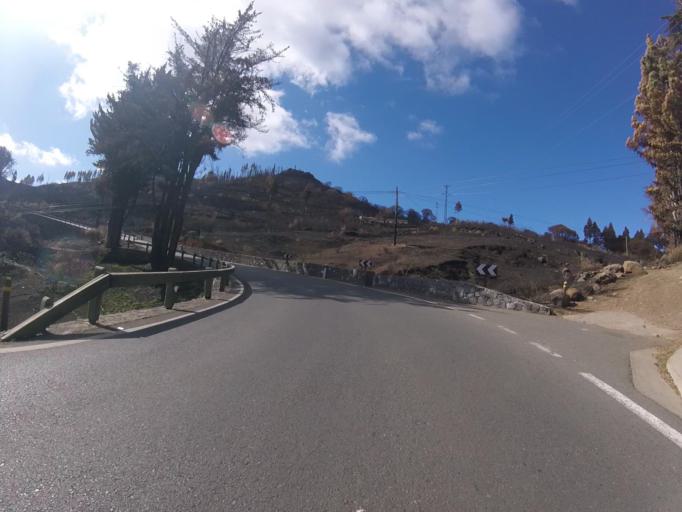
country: ES
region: Canary Islands
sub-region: Provincia de Las Palmas
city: Tejeda
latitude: 28.0062
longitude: -15.5967
